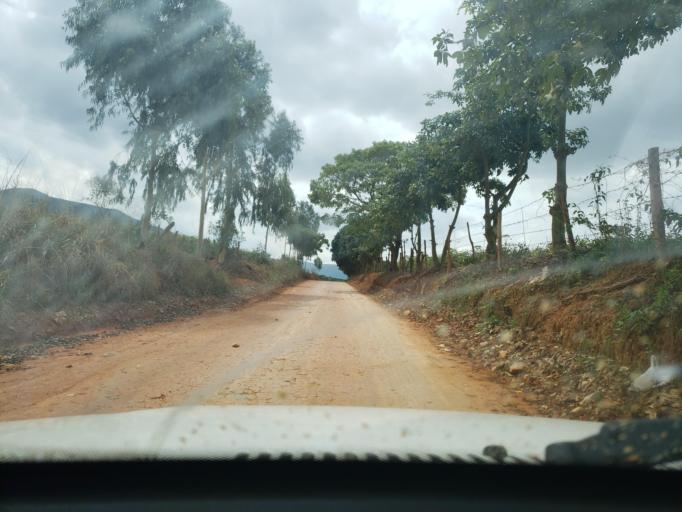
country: BR
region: Minas Gerais
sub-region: Boa Esperanca
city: Boa Esperanca
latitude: -20.9927
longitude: -45.5958
